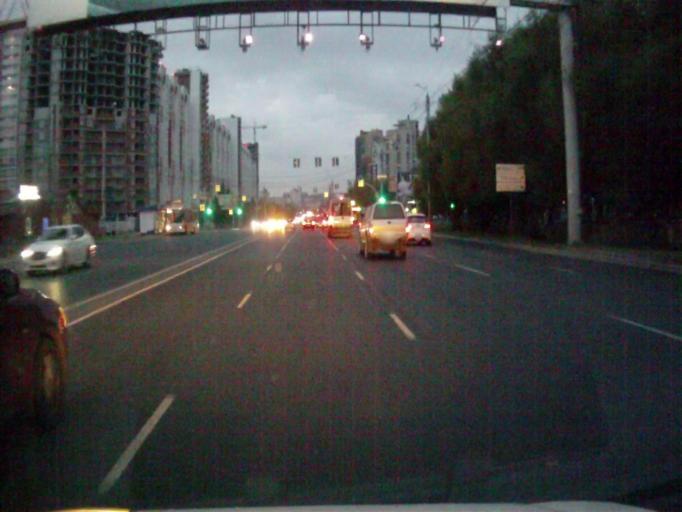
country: RU
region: Chelyabinsk
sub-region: Gorod Chelyabinsk
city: Chelyabinsk
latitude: 55.1772
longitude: 61.3129
